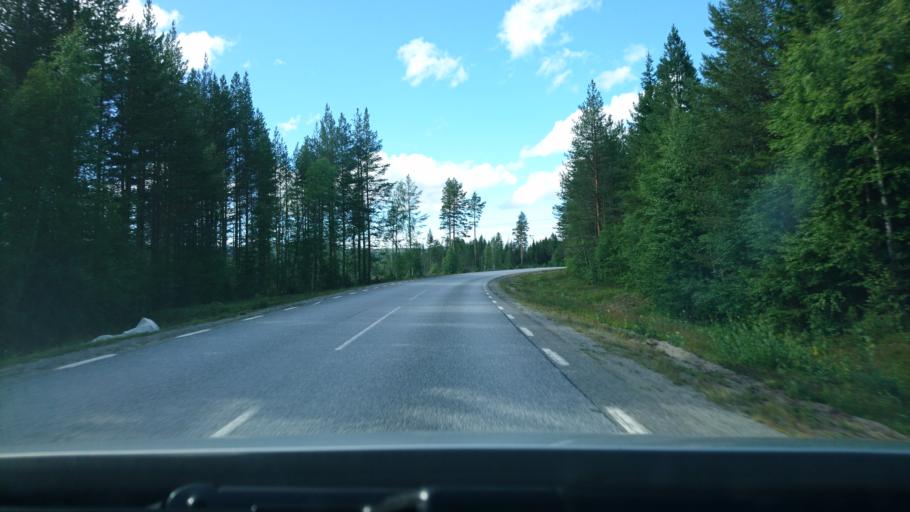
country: SE
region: Vaesterbotten
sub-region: Asele Kommun
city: Asele
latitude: 64.2521
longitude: 17.2737
